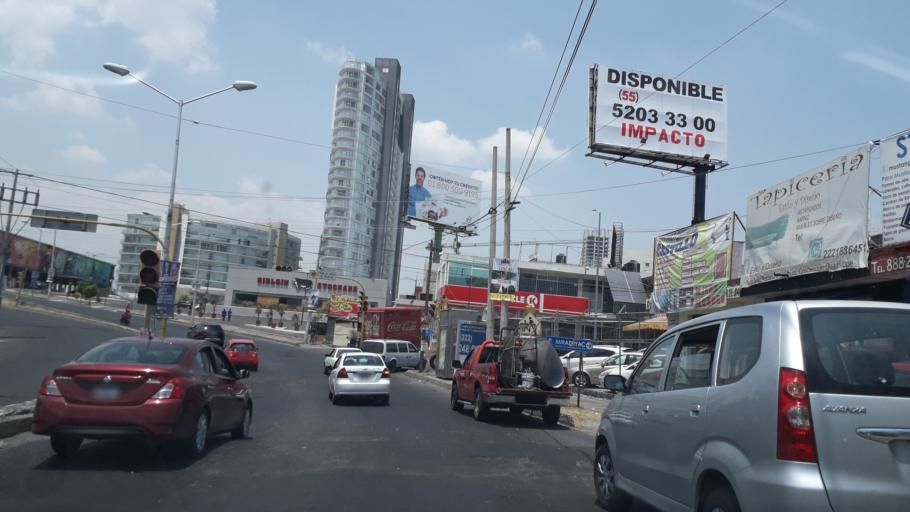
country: MX
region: Puebla
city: Puebla
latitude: 19.0277
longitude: -98.2268
